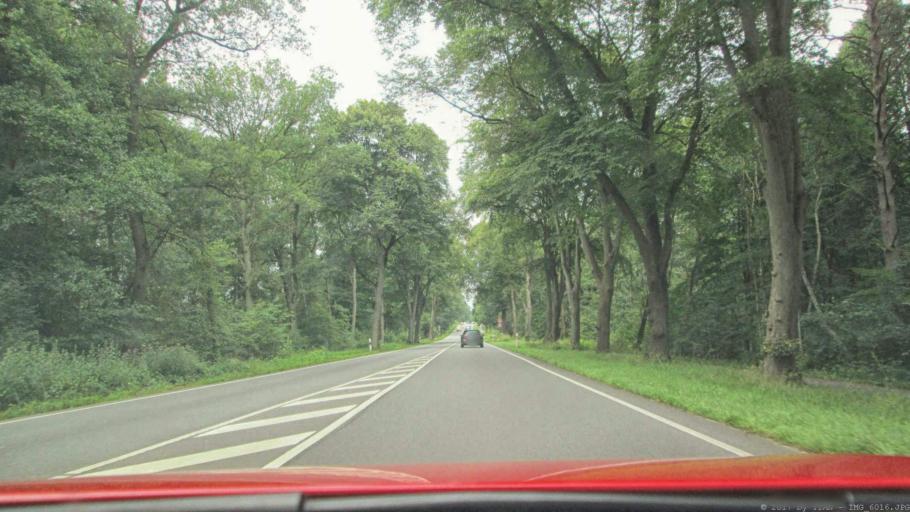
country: DE
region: Lower Saxony
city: Melbeck
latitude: 53.1703
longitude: 10.4266
